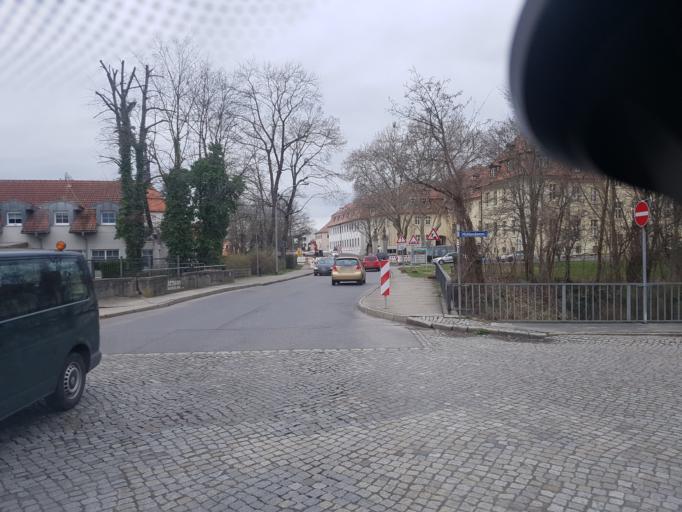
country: DE
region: Brandenburg
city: Luebben
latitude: 51.9407
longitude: 13.9015
